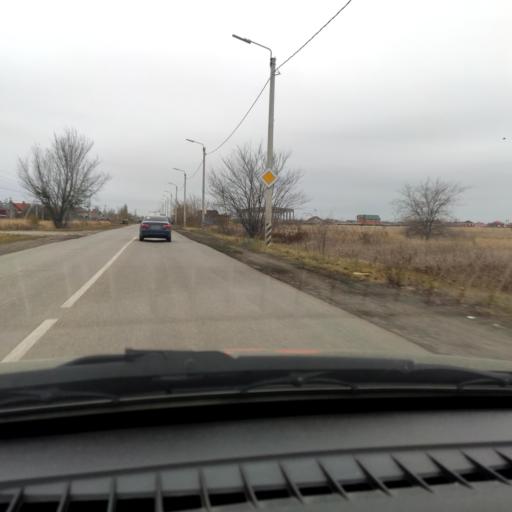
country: RU
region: Samara
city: Podstepki
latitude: 53.5221
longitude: 49.1753
